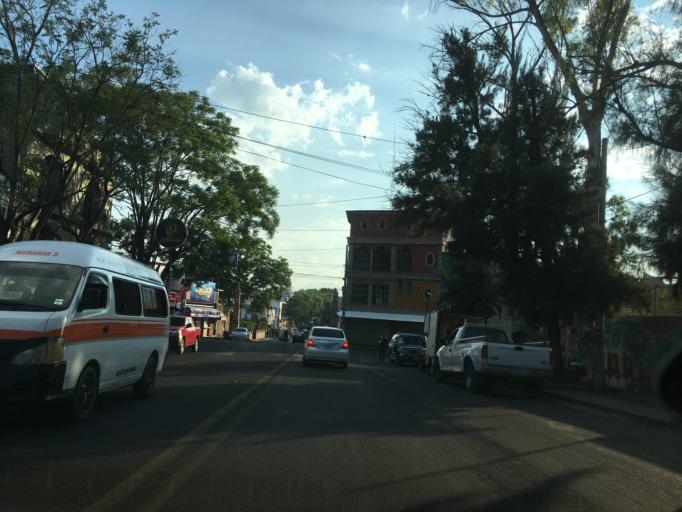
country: MX
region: Michoacan
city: Morelia
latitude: 19.7055
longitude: -101.1764
